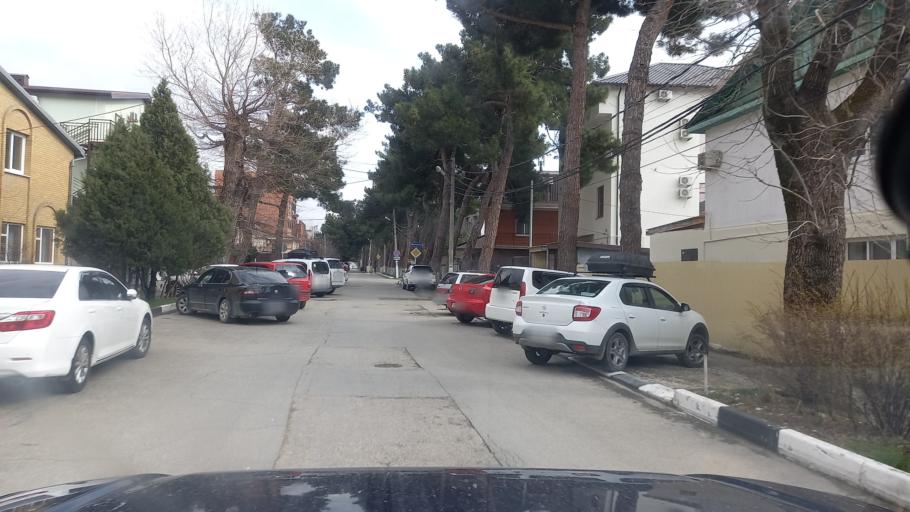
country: RU
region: Krasnodarskiy
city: Gelendzhik
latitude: 44.5609
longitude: 38.0843
